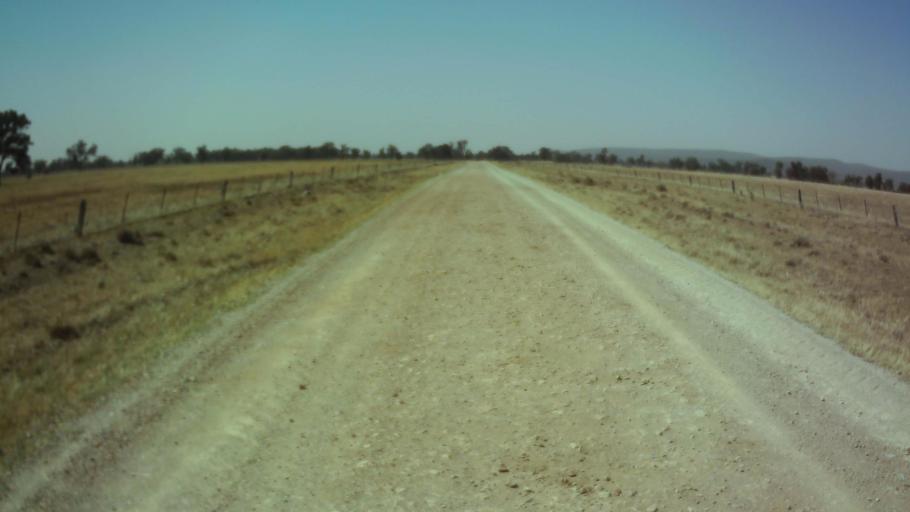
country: AU
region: New South Wales
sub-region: Weddin
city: Grenfell
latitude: -34.0318
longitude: 147.9123
